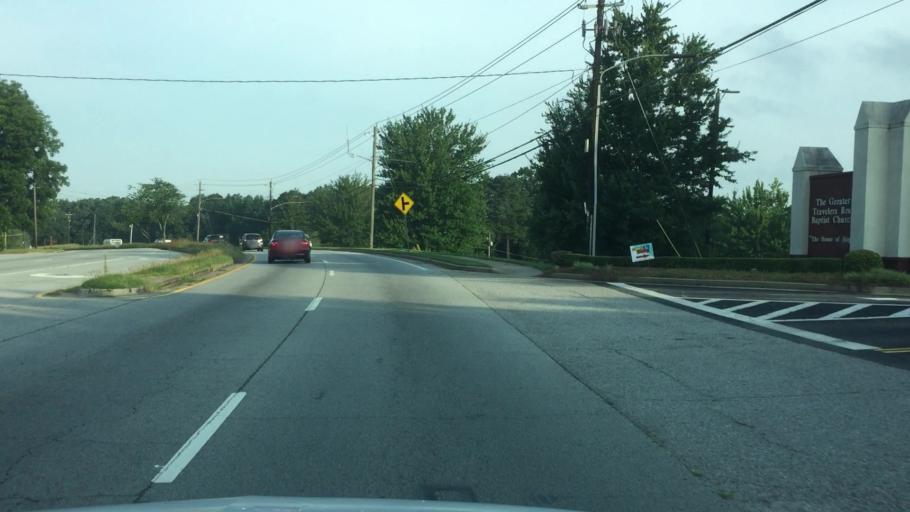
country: US
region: Georgia
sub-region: DeKalb County
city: Panthersville
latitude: 33.6834
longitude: -84.2336
